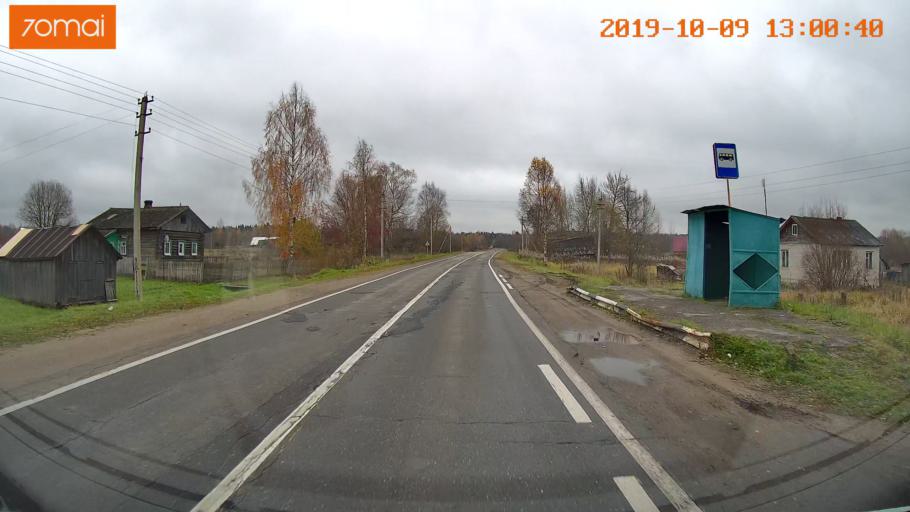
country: RU
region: Jaroslavl
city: Prechistoye
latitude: 58.3750
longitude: 40.4822
